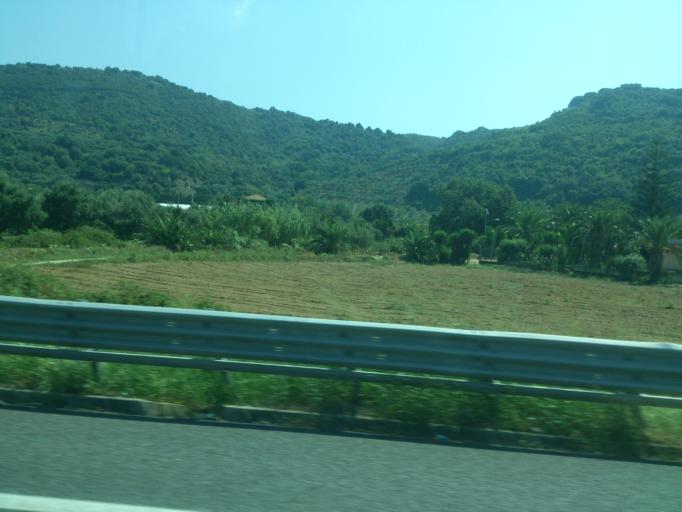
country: IT
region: Calabria
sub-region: Provincia di Vibo-Valentia
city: Francavilla Angitola
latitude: 38.7951
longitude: 16.2249
